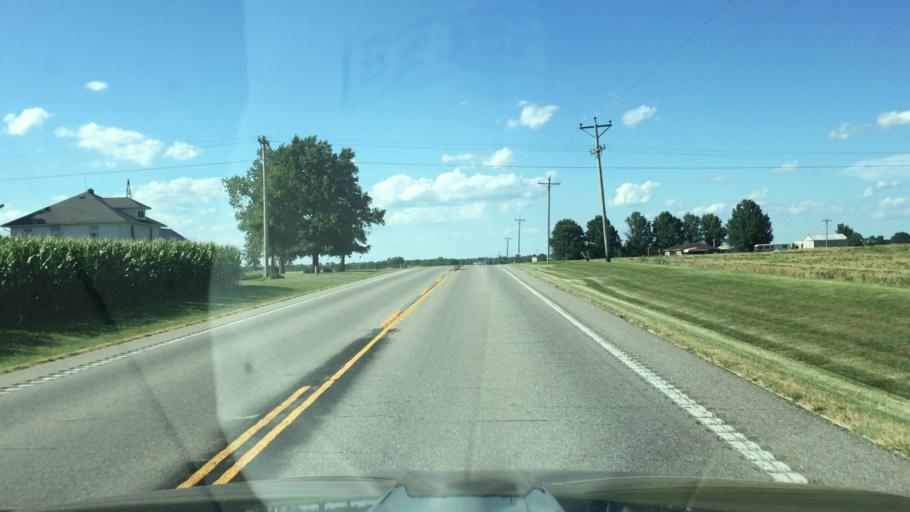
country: US
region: Missouri
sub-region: Moniteau County
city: Tipton
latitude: 38.6117
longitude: -92.7902
